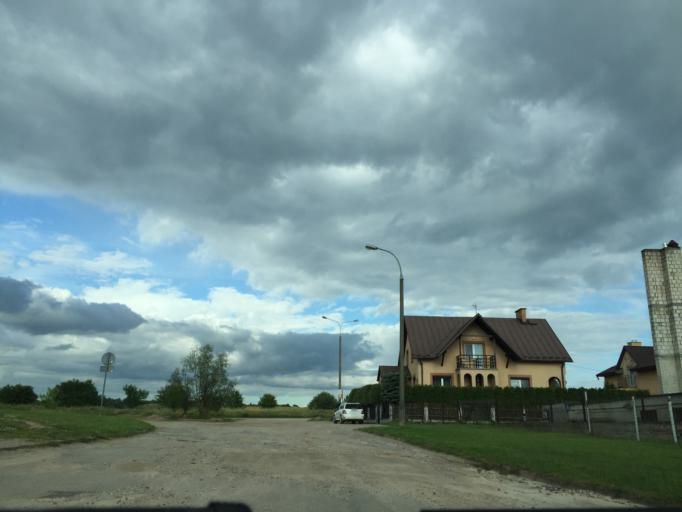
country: PL
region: Podlasie
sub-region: Suwalki
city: Suwalki
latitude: 54.1212
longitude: 22.9509
